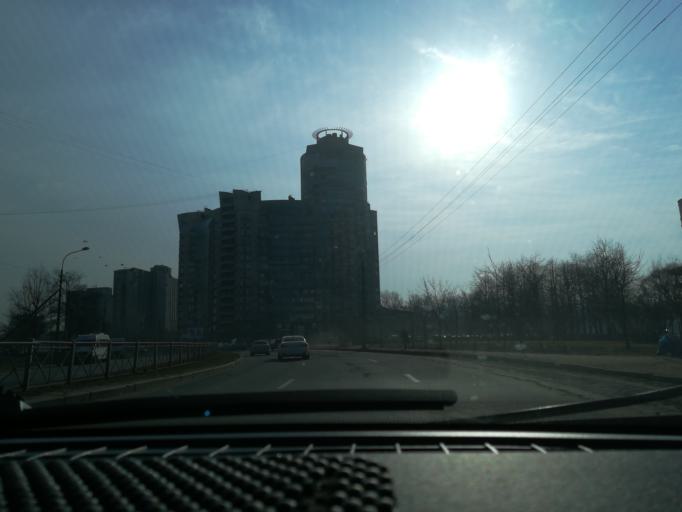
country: RU
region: St.-Petersburg
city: Vasyl'evsky Ostrov
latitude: 59.9475
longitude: 30.2370
